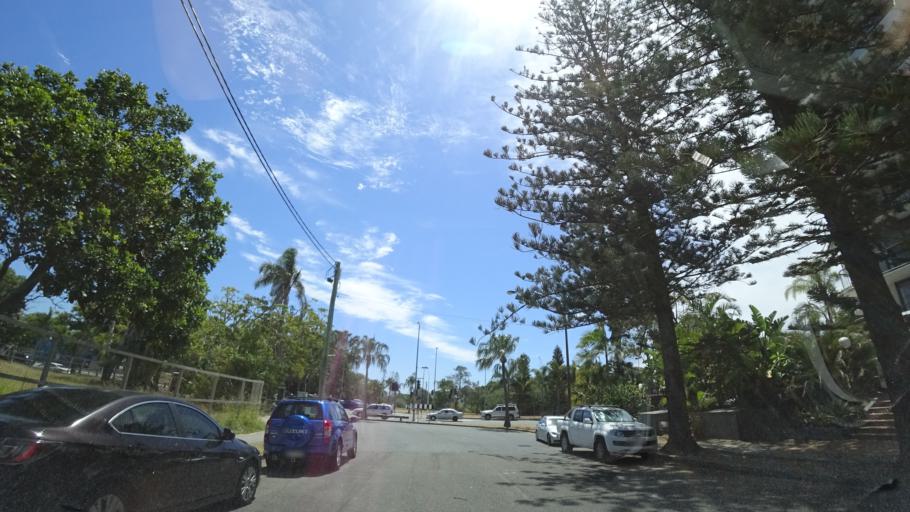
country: AU
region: Queensland
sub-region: Gold Coast
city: Surfers Paradise
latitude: -28.0086
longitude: 153.4283
